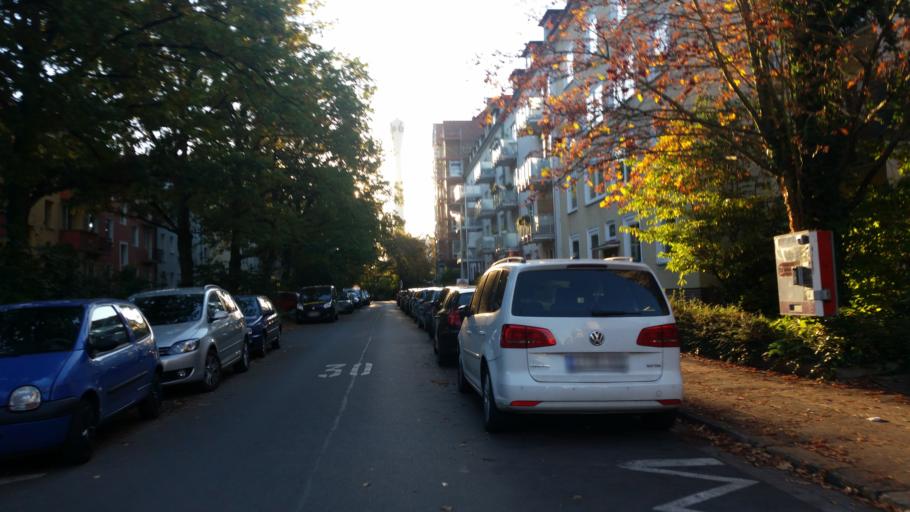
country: DE
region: Lower Saxony
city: Hannover
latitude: 52.3609
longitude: 9.7451
